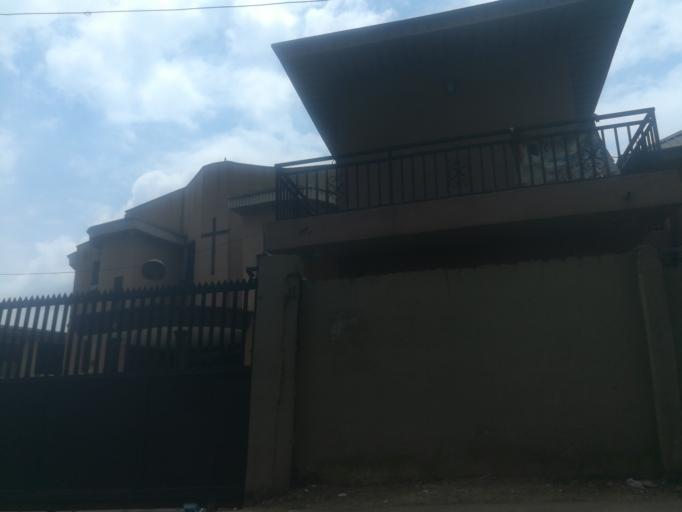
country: NG
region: Lagos
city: Ojota
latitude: 6.5907
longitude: 3.3882
